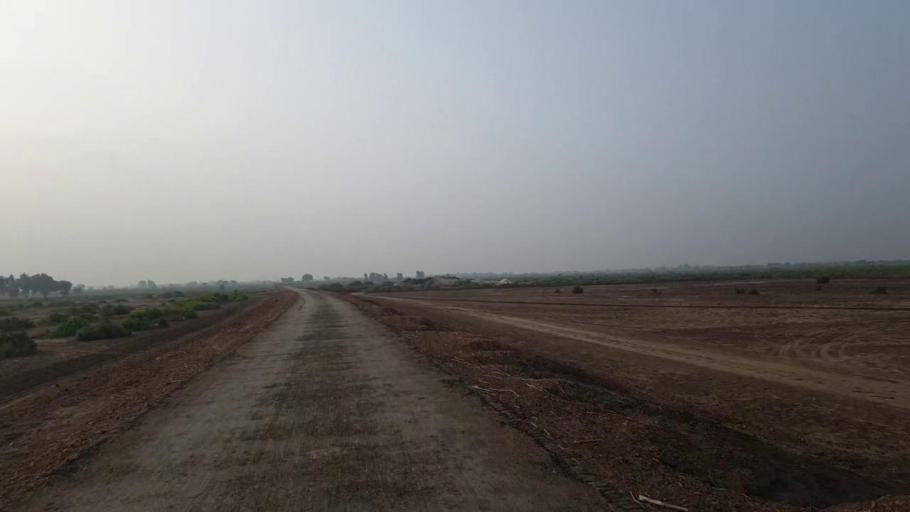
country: PK
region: Sindh
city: Tando Muhammad Khan
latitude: 25.1596
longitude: 68.6098
